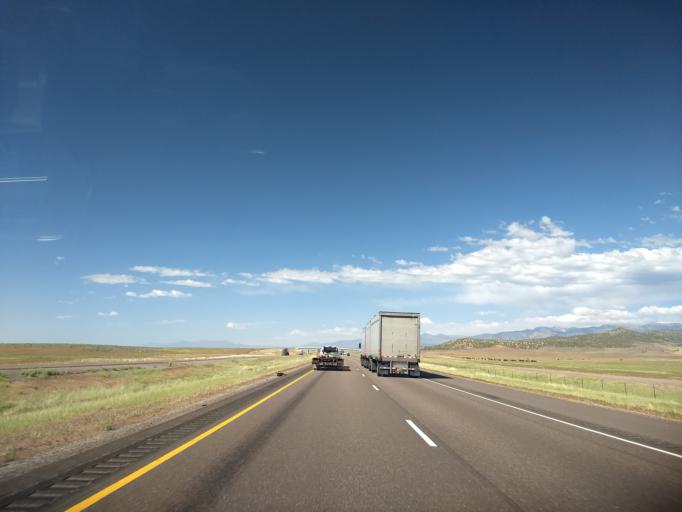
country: US
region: Utah
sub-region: Millard County
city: Fillmore
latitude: 38.7402
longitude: -112.5822
